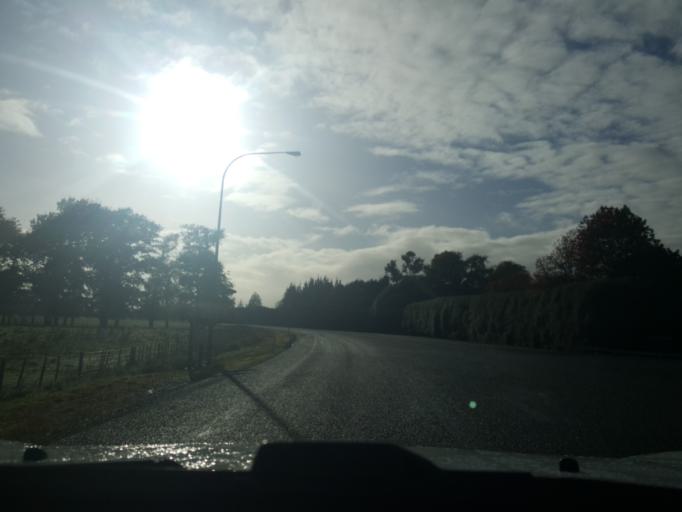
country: NZ
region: Waikato
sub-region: Waipa District
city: Cambridge
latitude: -37.7788
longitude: 175.4008
